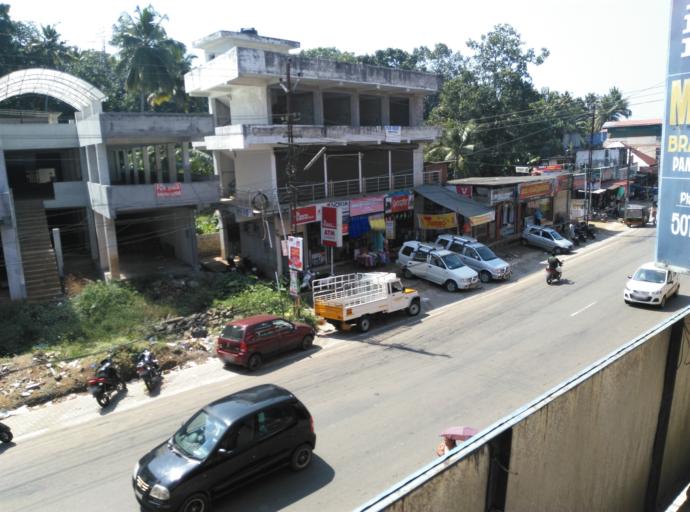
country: IN
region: Kerala
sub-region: Kottayam
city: Kottayam
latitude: 9.5718
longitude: 76.6407
